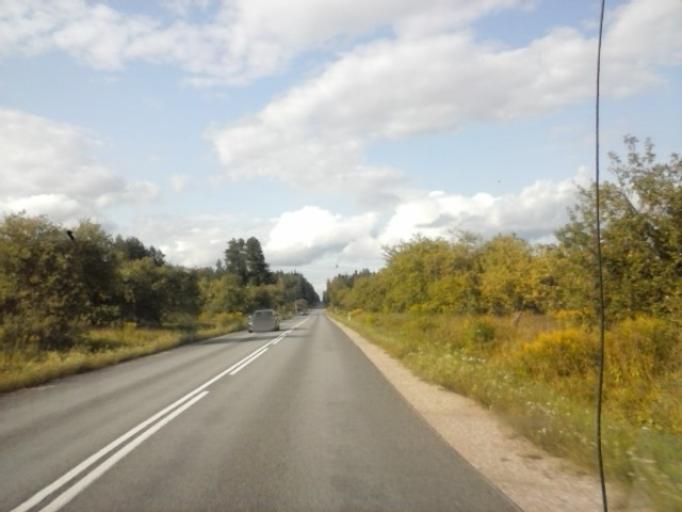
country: LV
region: Valmieras Rajons
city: Valmiera
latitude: 57.4821
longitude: 25.4091
